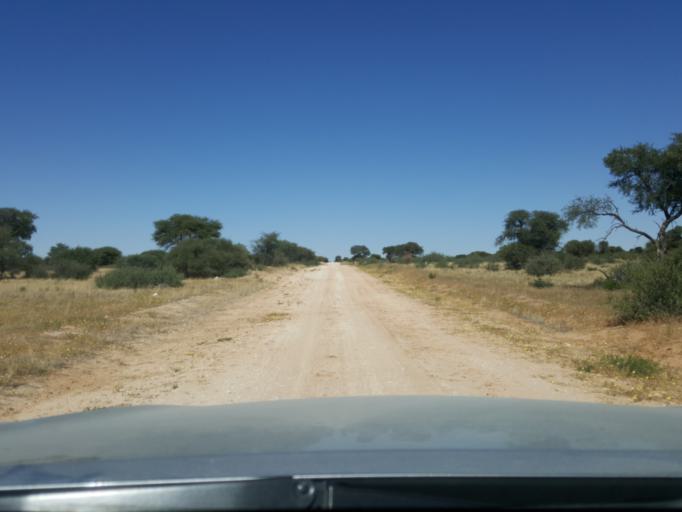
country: BW
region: Kgalagadi
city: Hukuntsi
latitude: -24.0211
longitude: 21.2159
